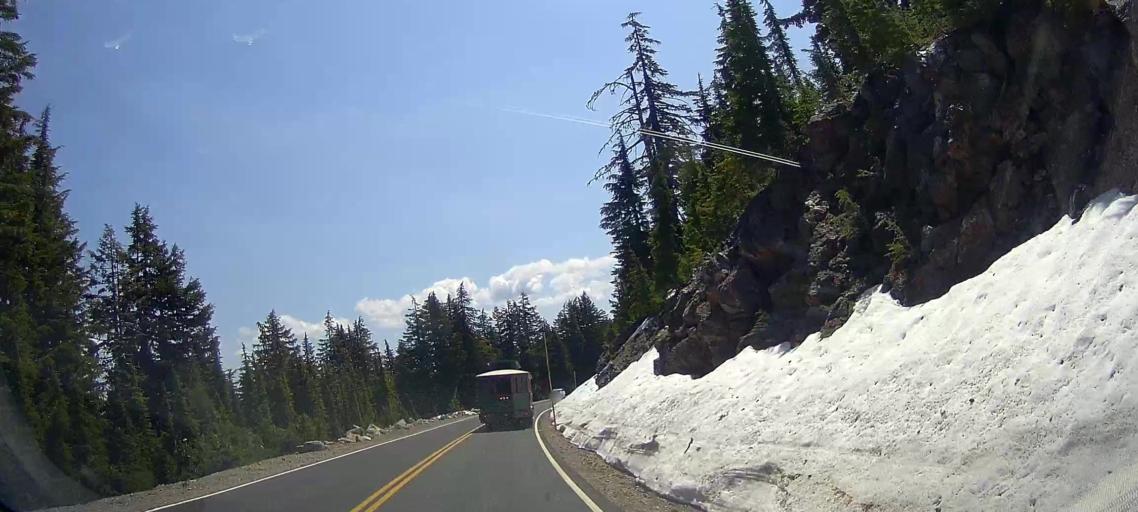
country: US
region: Oregon
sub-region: Jackson County
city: Shady Cove
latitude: 42.9823
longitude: -122.1325
